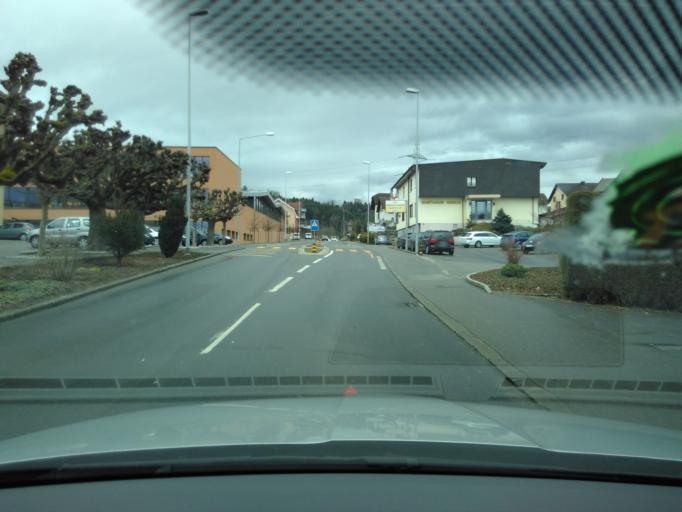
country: CH
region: Lucerne
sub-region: Hochdorf District
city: Inwil
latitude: 47.1227
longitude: 8.3537
